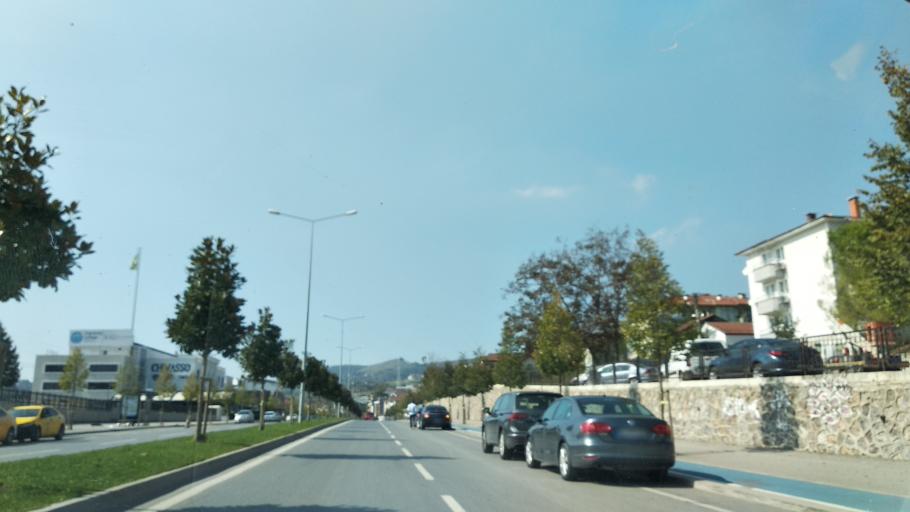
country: TR
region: Sakarya
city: Adapazari
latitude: 40.7600
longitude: 30.3608
